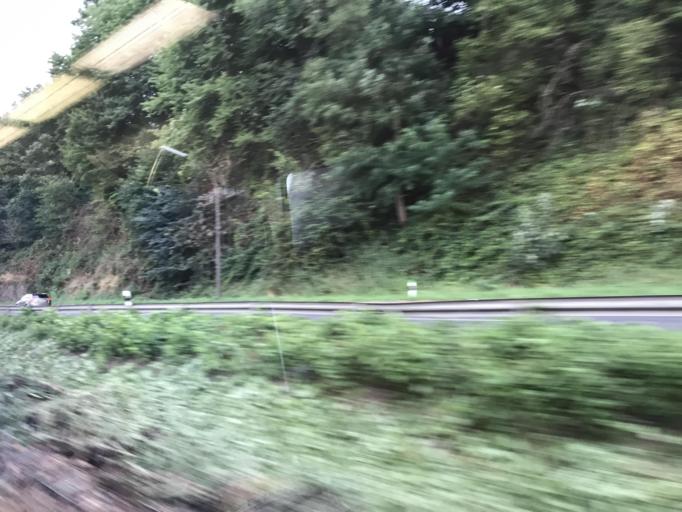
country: DE
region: North Rhine-Westphalia
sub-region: Regierungsbezirk Koln
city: Eitorf
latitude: 50.7764
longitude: 7.4349
